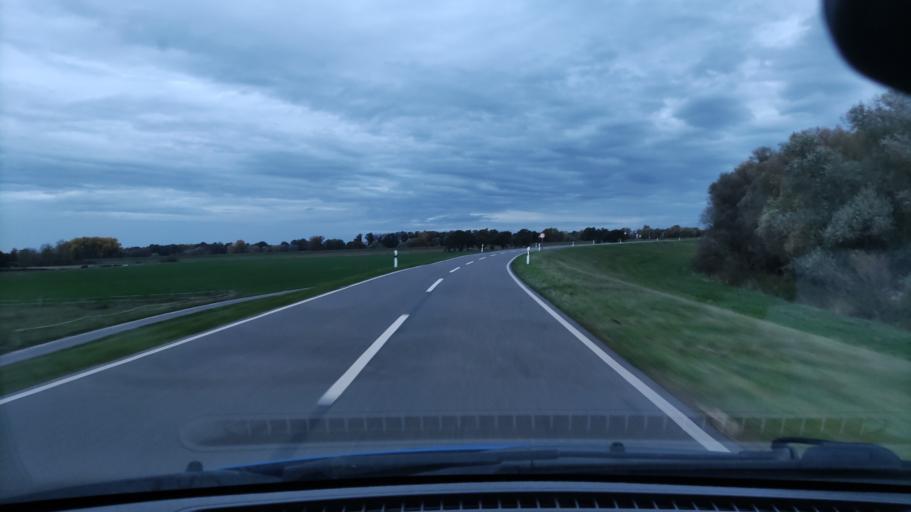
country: DE
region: Lower Saxony
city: Gorleben
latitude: 53.0539
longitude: 11.3893
